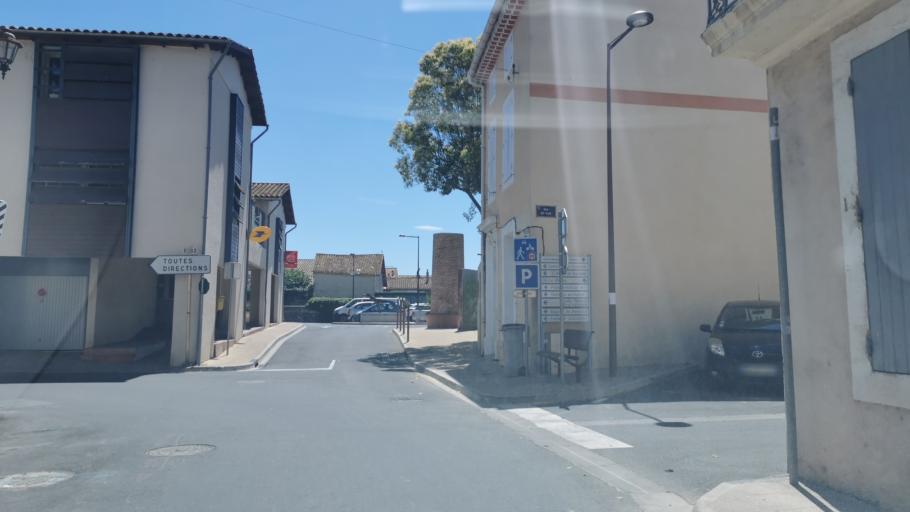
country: FR
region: Languedoc-Roussillon
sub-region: Departement de l'Herault
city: Nissan-lez-Enserune
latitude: 43.2896
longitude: 3.1267
